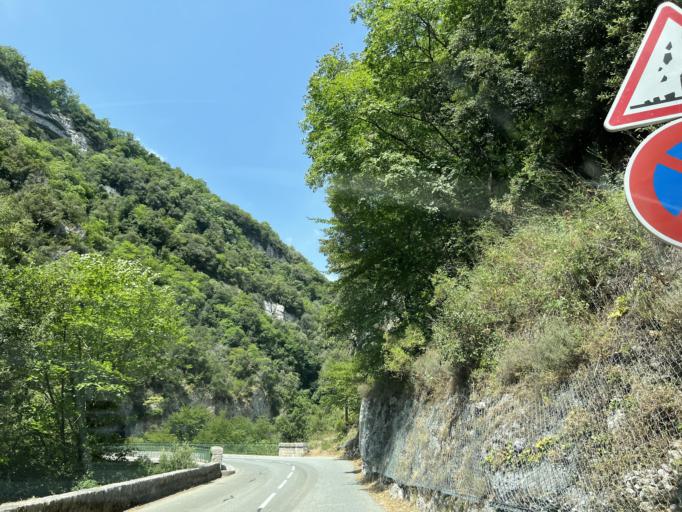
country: FR
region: Provence-Alpes-Cote d'Azur
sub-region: Departement des Alpes-Maritimes
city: Tourrettes-sur-Loup
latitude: 43.7424
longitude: 6.9999
